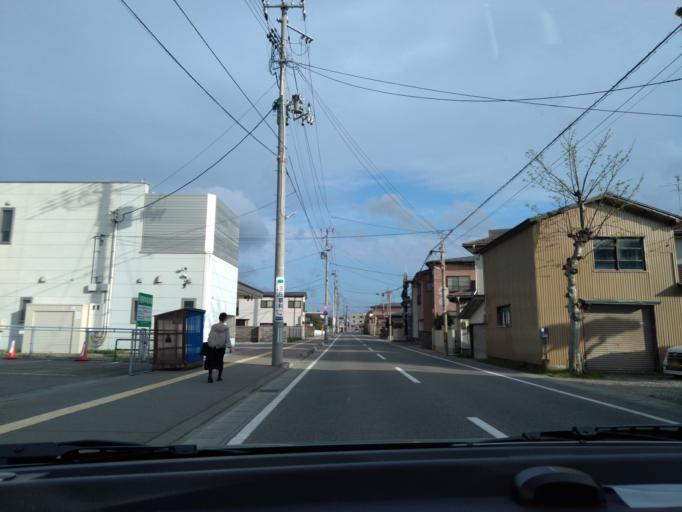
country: JP
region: Akita
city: Akita Shi
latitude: 39.7578
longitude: 140.0733
